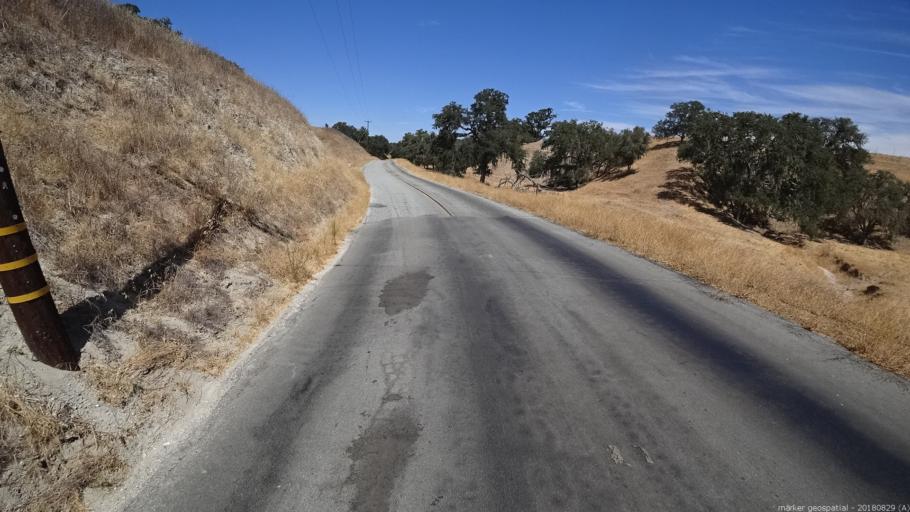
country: US
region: California
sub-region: San Luis Obispo County
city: Lake Nacimiento
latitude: 35.8596
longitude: -120.8409
